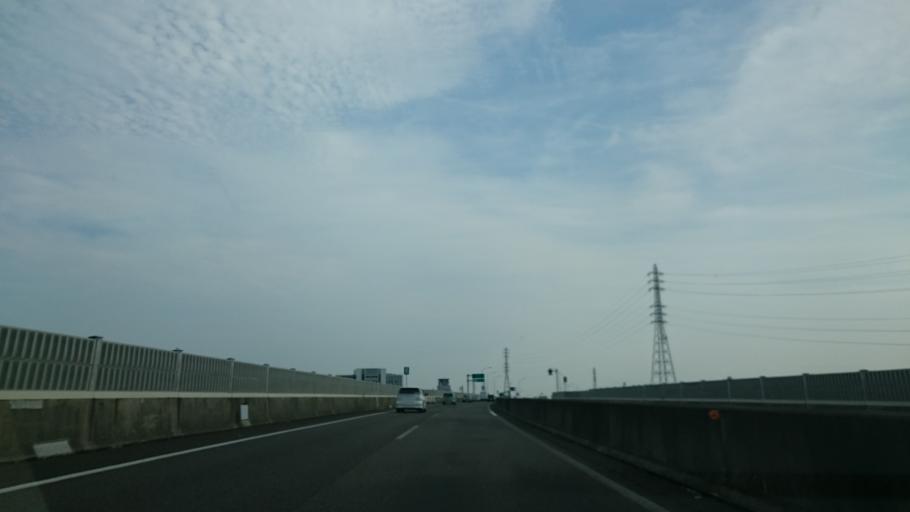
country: JP
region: Aichi
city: Ichinomiya
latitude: 35.3198
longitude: 136.7790
